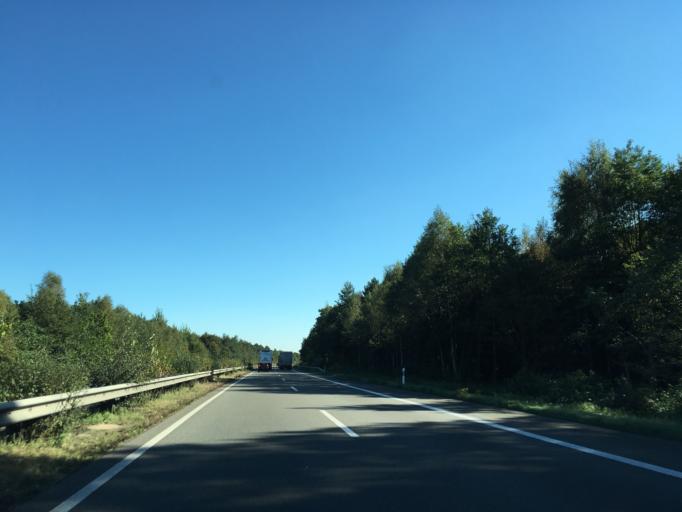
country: DE
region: Lower Saxony
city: Radbruch
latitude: 53.3281
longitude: 10.2835
